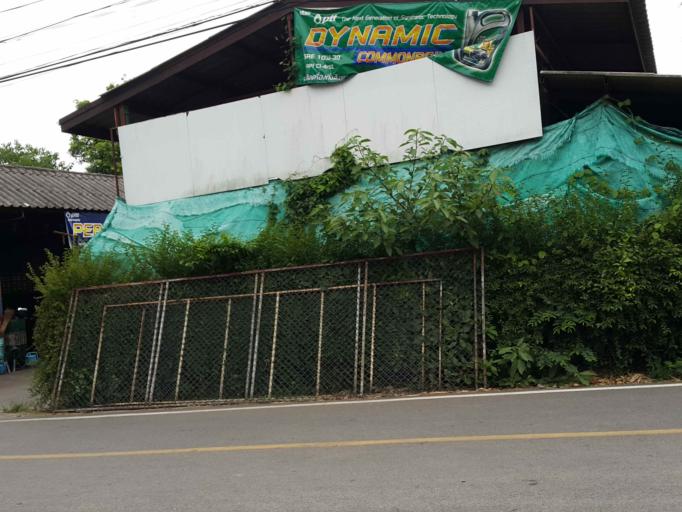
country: TH
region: Chiang Mai
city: Chiang Mai
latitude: 18.7491
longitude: 99.0012
